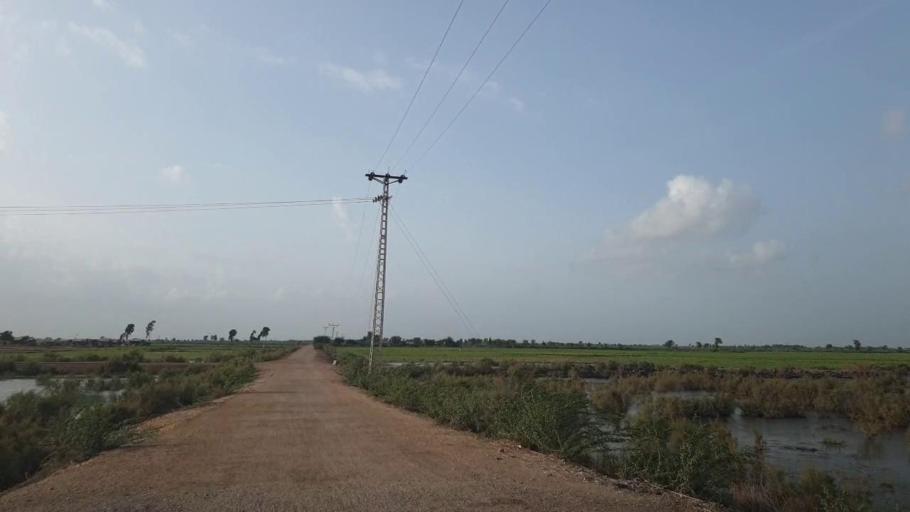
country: PK
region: Sindh
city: Tando Bago
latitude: 24.6561
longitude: 69.1119
